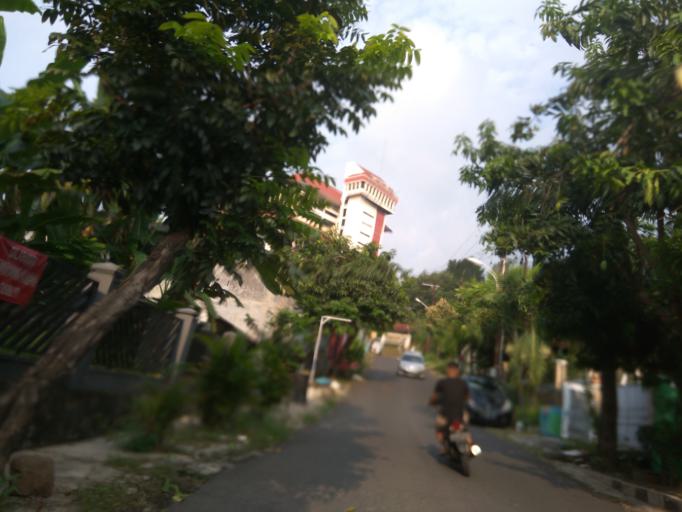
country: ID
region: Central Java
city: Semarang
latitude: -7.0164
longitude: 110.3952
